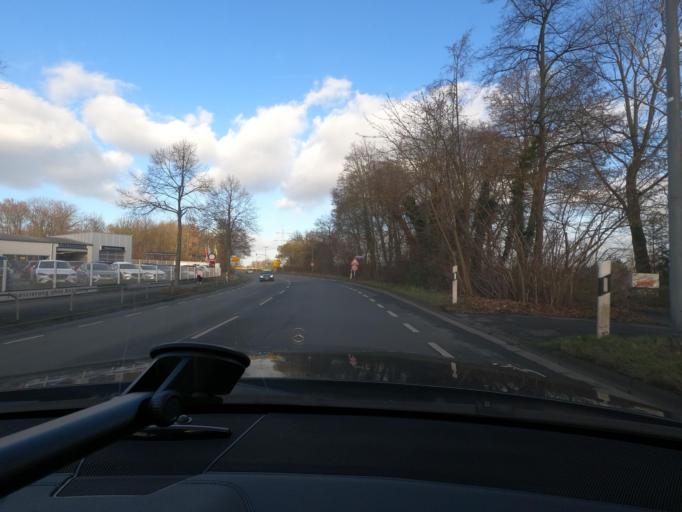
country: DE
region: North Rhine-Westphalia
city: Schwerte
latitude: 51.5001
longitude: 7.5739
